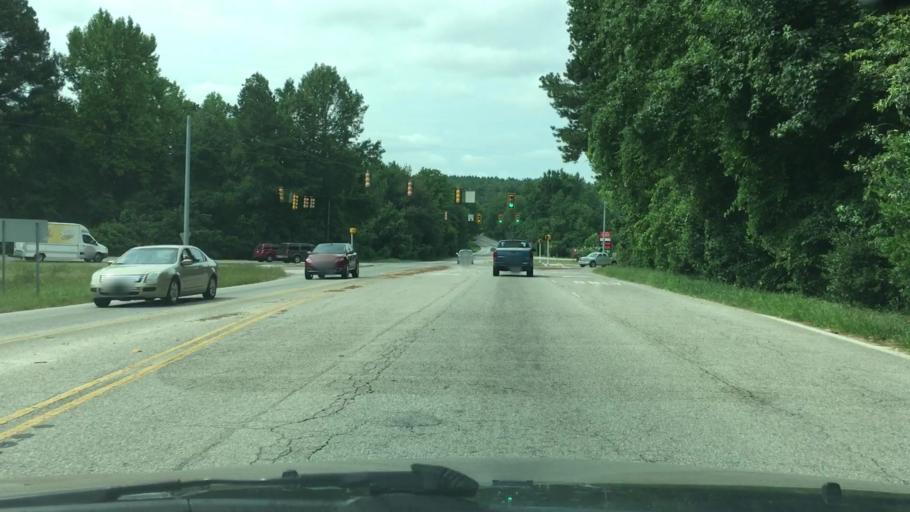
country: US
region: South Carolina
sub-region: Aiken County
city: Warrenville
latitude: 33.5594
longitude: -81.7787
